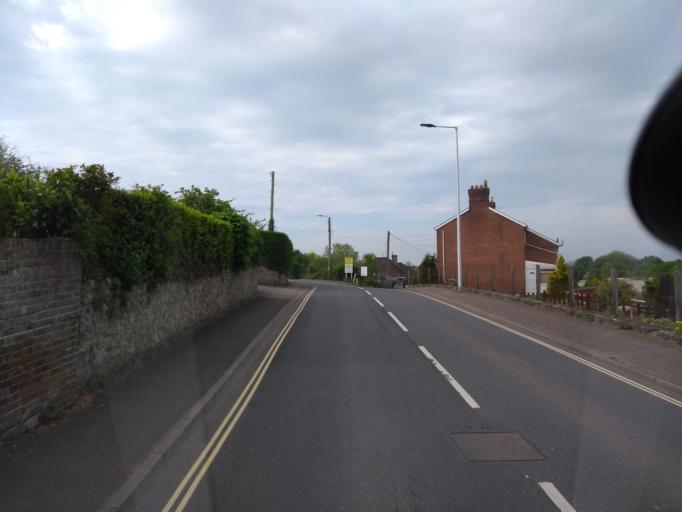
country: GB
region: England
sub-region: Devon
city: Axminster
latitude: 50.7794
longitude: -3.0027
